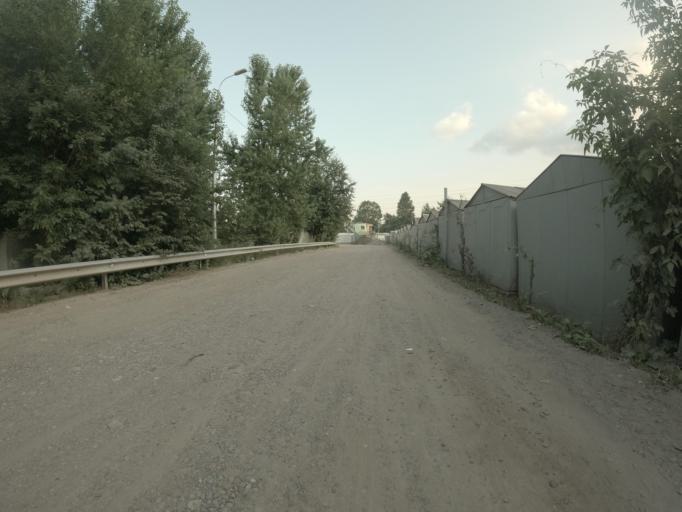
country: RU
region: St.-Petersburg
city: Krasnogvargeisky
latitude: 59.9560
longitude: 30.4566
